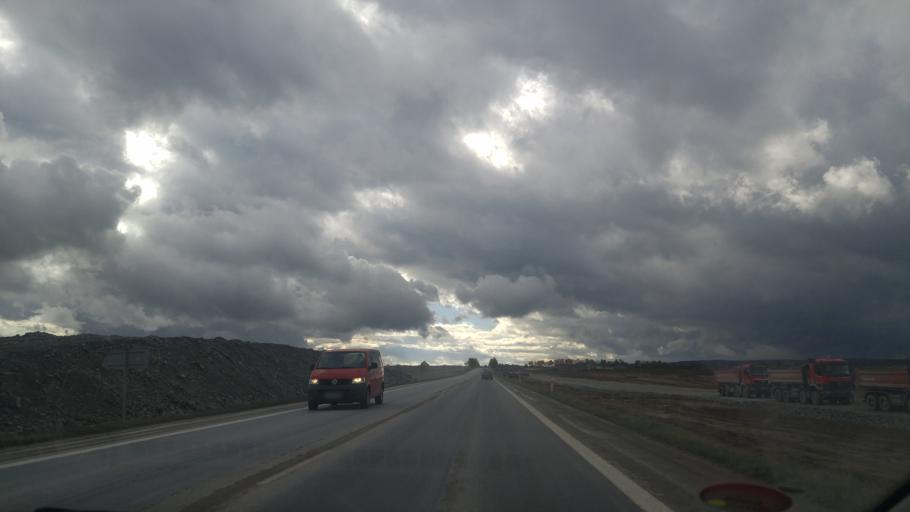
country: CZ
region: Jihocesky
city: Dolni Bukovsko
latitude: 49.1406
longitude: 14.6191
